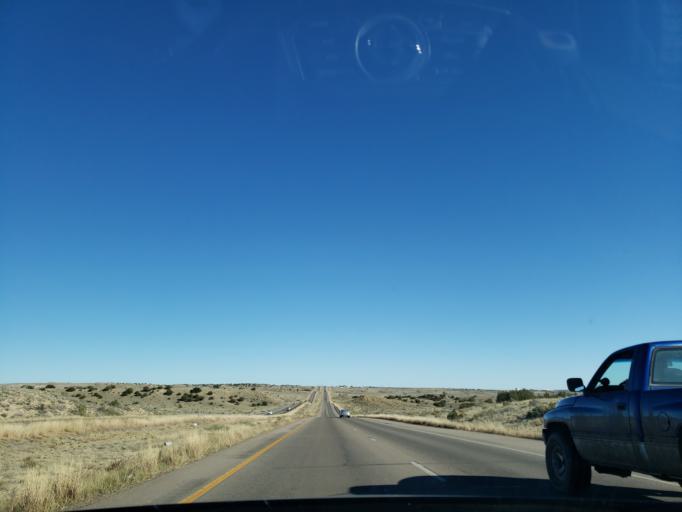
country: US
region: Colorado
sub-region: Fremont County
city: Florence
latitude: 38.4452
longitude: -105.1451
